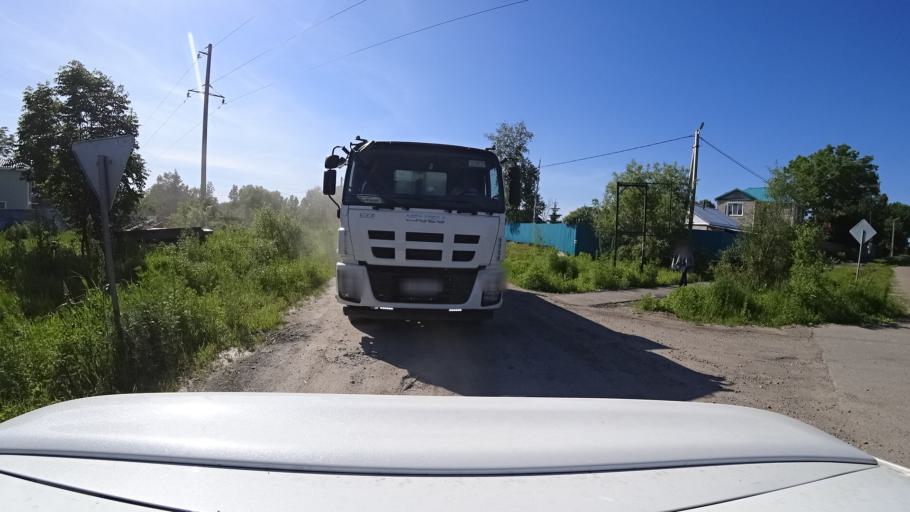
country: RU
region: Khabarovsk Krai
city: Topolevo
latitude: 48.5512
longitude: 135.1900
